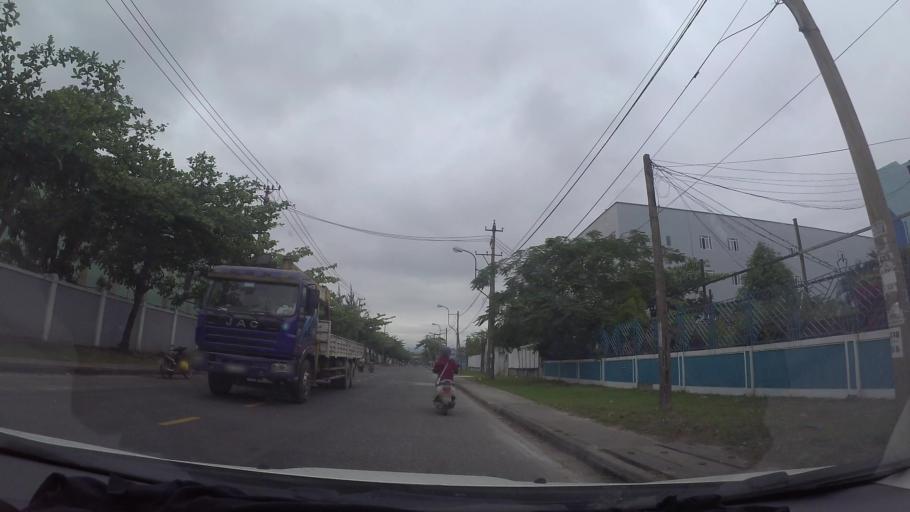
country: VN
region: Da Nang
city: Lien Chieu
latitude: 16.0813
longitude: 108.1422
